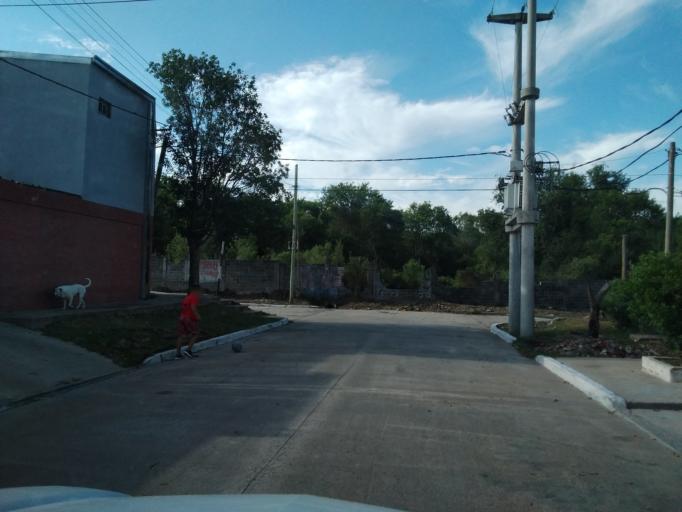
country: AR
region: Corrientes
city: Corrientes
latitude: -27.4623
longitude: -58.8136
